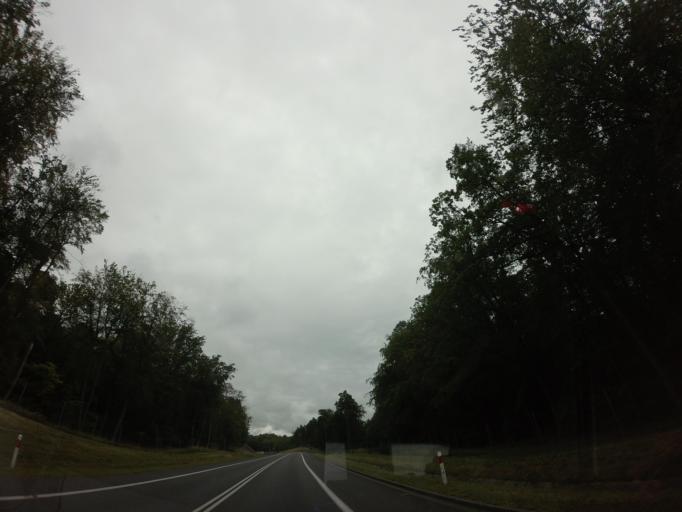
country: PL
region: West Pomeranian Voivodeship
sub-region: Powiat kamienski
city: Miedzyzdroje
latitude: 53.9048
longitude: 14.4467
